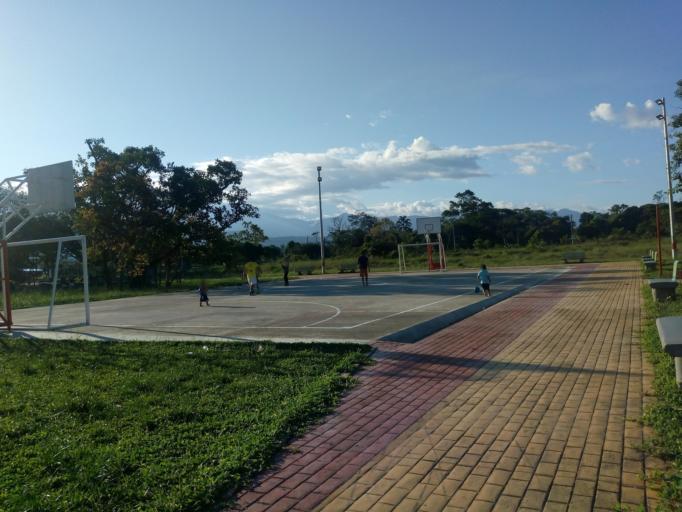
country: CO
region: Putumayo
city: Villagarzon
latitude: 1.0084
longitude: -76.6130
